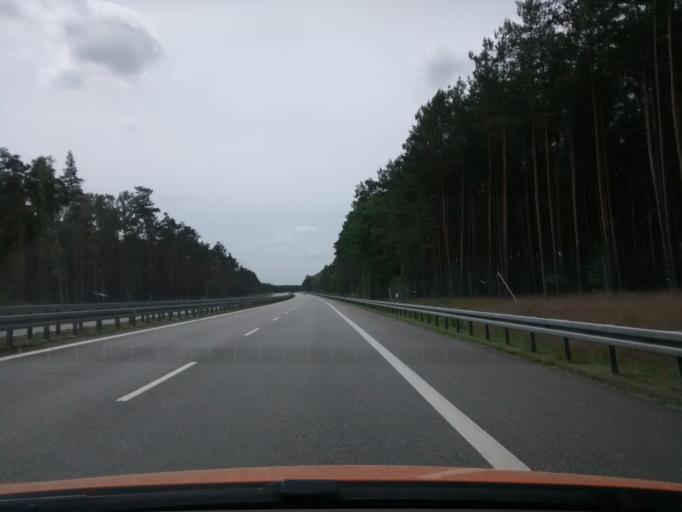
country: DE
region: Brandenburg
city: Trebbin
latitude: 52.1446
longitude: 13.2337
